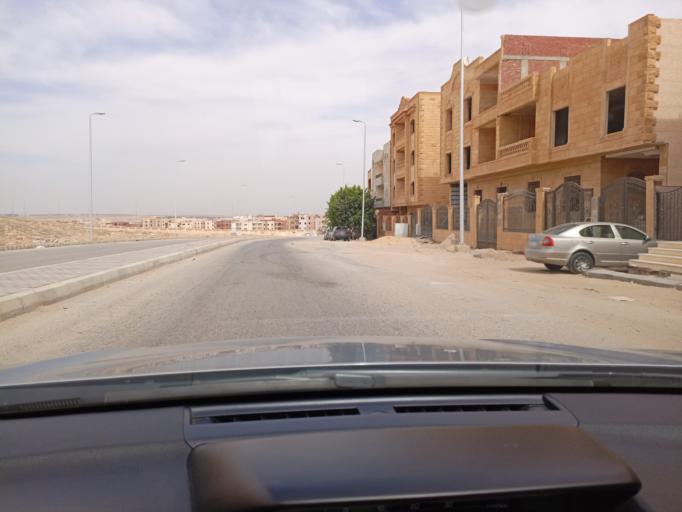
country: EG
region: Muhafazat al Qalyubiyah
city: Al Khankah
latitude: 30.2452
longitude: 31.4907
